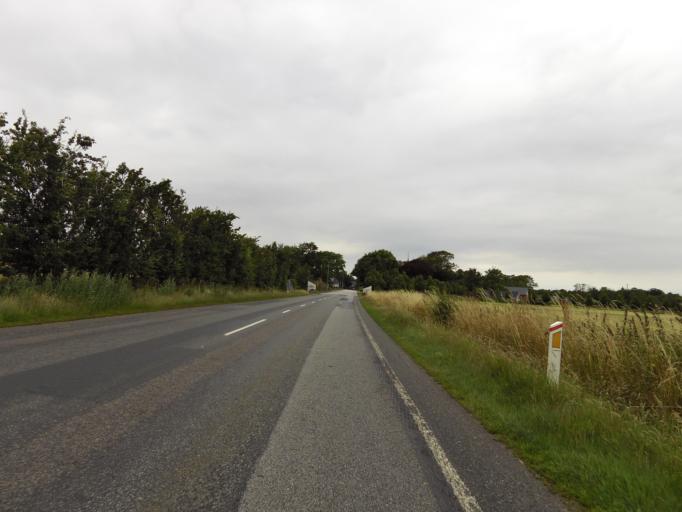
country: DK
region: South Denmark
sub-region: Tonder Kommune
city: Logumkloster
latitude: 55.1463
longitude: 8.9627
